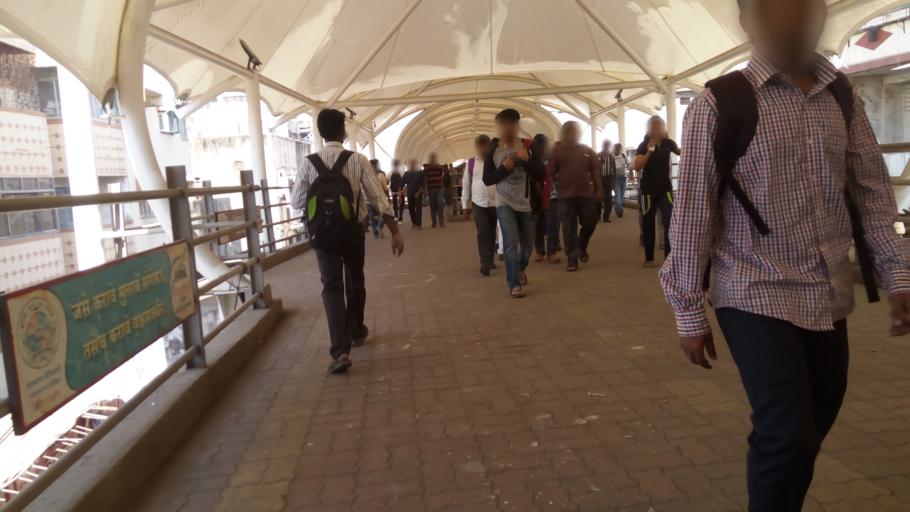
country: IN
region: Maharashtra
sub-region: Thane
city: Dombivli
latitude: 19.2176
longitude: 73.0887
